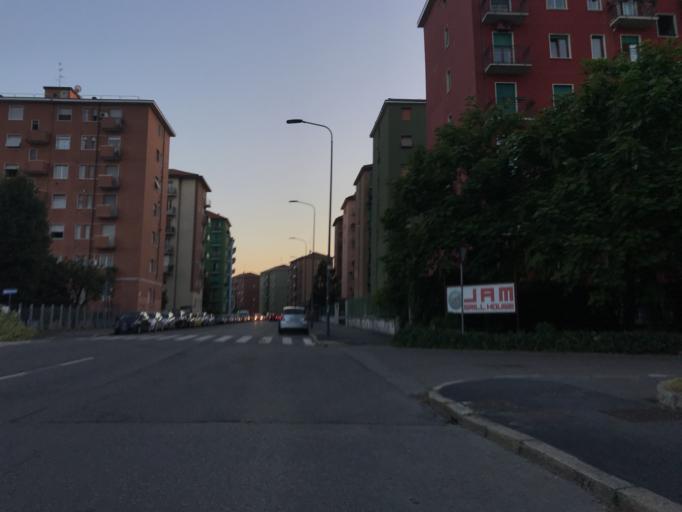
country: IT
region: Lombardy
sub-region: Citta metropolitana di Milano
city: Sesto San Giovanni
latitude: 45.4978
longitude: 9.2397
